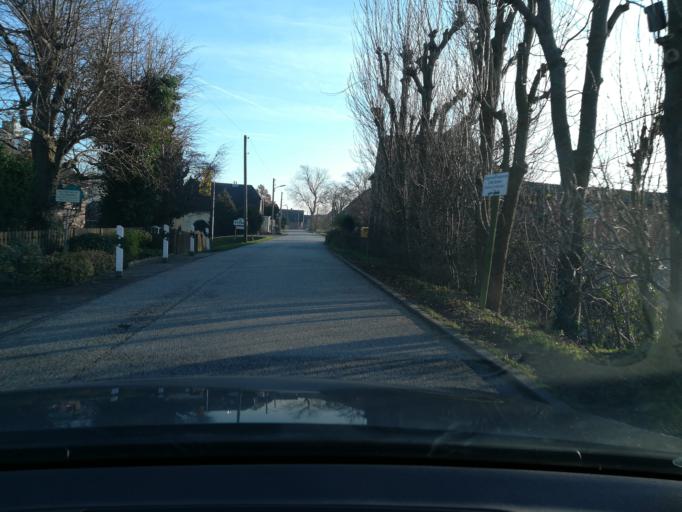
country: DE
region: Lower Saxony
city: Stelle
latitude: 53.4462
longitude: 10.1084
